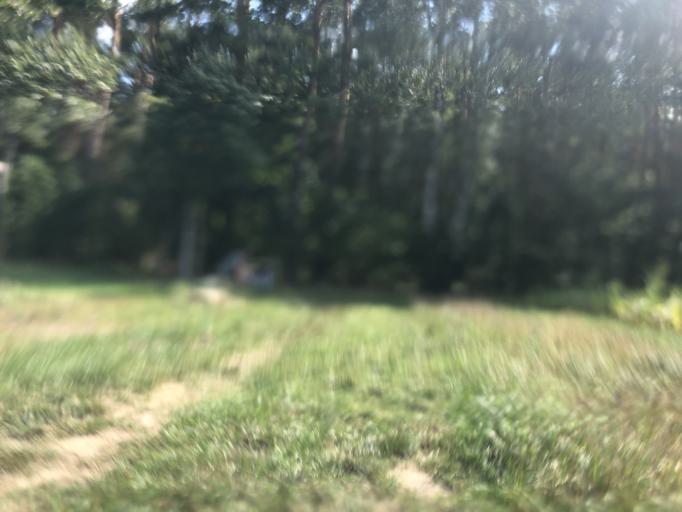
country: DE
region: Brandenburg
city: Mullrose
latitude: 52.2341
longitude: 14.4050
